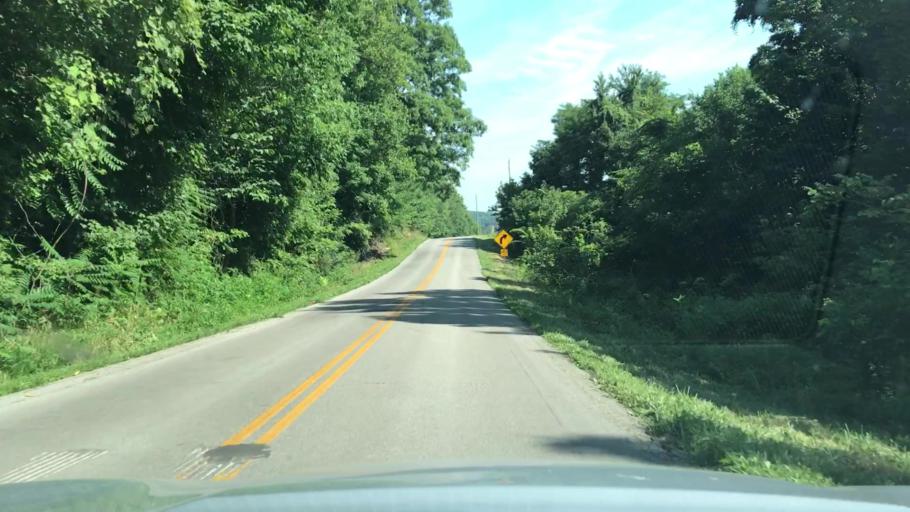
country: US
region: Kentucky
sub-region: Clinton County
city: Albany
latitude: 36.7314
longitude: -85.0138
